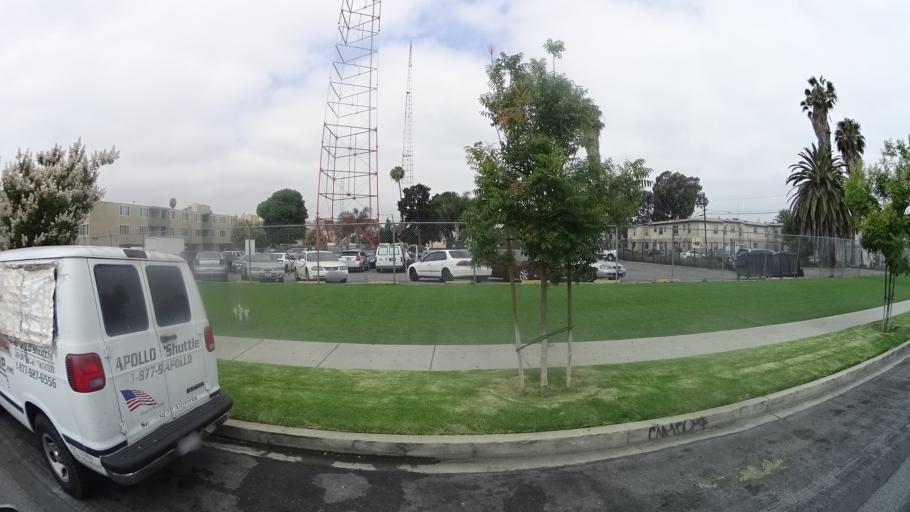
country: US
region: California
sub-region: Los Angeles County
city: View Park-Windsor Hills
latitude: 34.0197
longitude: -118.3452
